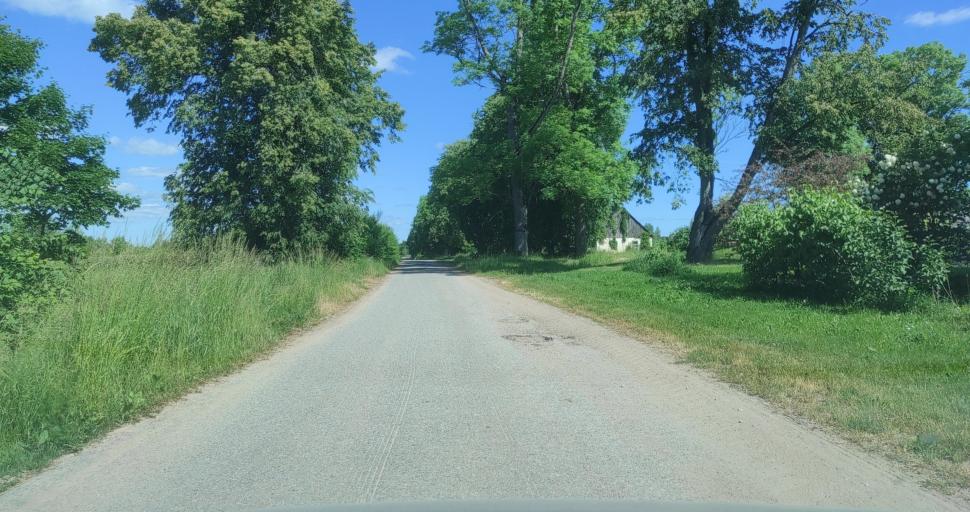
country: LV
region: Kuldigas Rajons
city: Kuldiga
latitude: 56.9368
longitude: 21.8256
